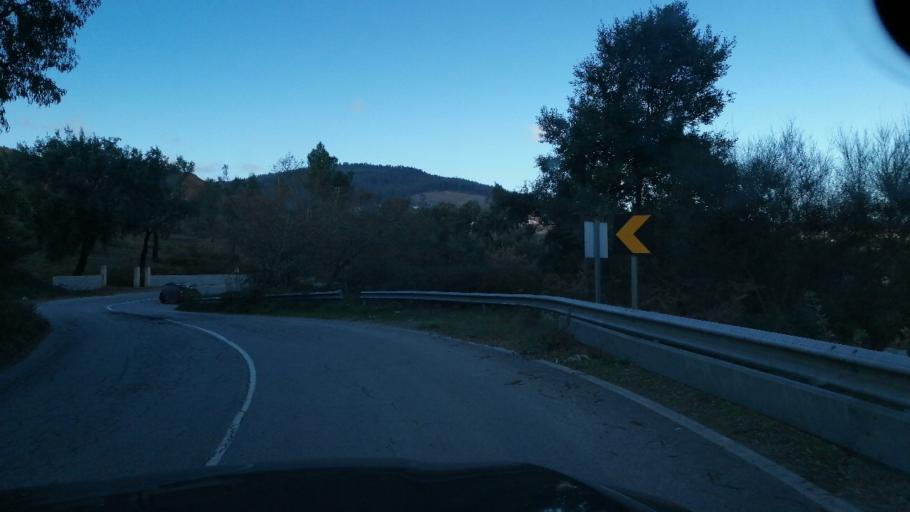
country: PT
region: Vila Real
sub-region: Mondim de Basto
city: Mondim de Basto
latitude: 41.4403
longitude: -7.9713
